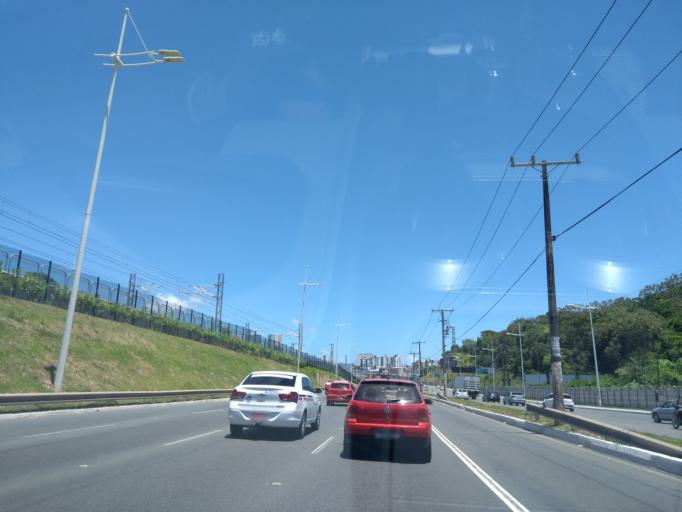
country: BR
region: Bahia
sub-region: Salvador
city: Salvador
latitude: -12.9728
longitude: -38.4475
